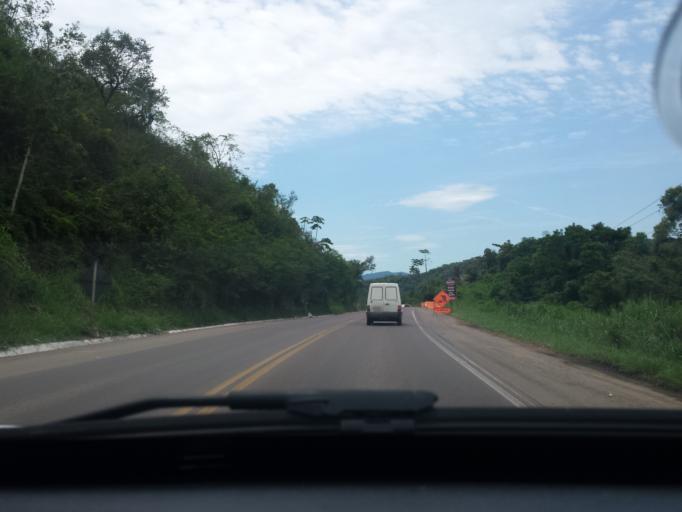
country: BR
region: Santa Catarina
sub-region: Gaspar
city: Gaspar
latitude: -26.8936
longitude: -48.9879
